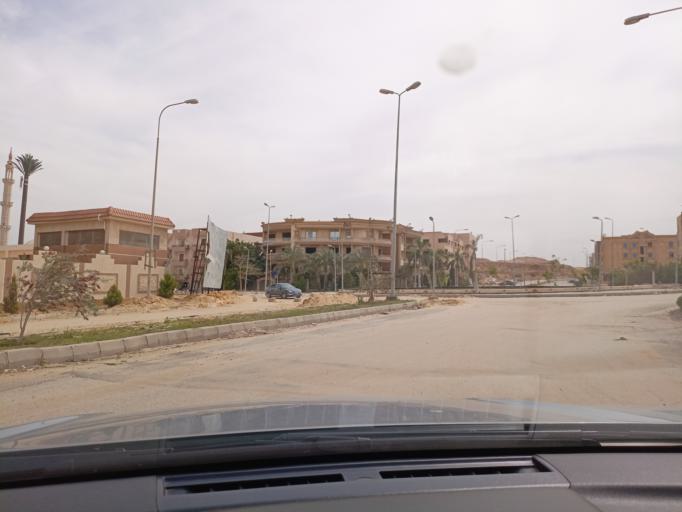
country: EG
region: Muhafazat al Qalyubiyah
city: Al Khankah
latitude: 30.2459
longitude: 31.4985
